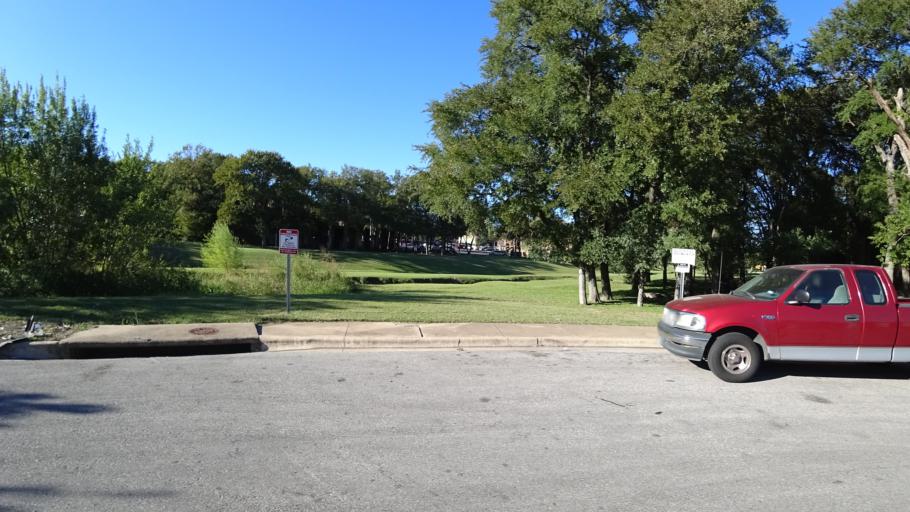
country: US
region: Texas
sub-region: Travis County
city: Austin
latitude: 30.2302
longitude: -97.7230
